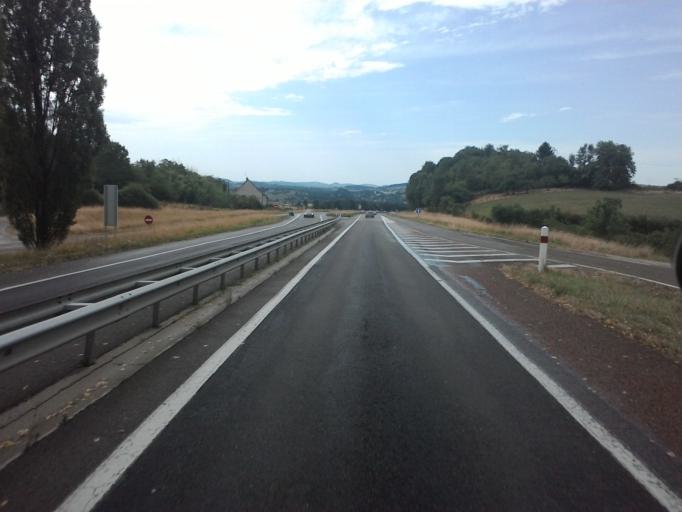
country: FR
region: Franche-Comte
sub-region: Departement du Jura
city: Bletterans
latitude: 46.7836
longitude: 5.5611
